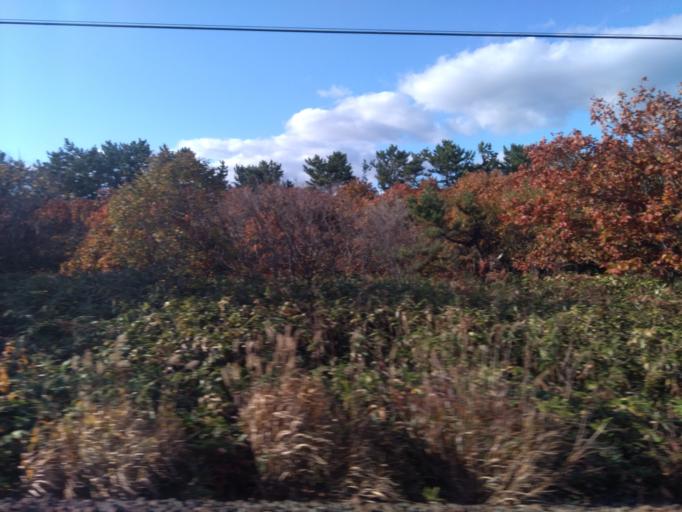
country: JP
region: Hokkaido
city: Niseko Town
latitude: 42.5703
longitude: 140.4415
